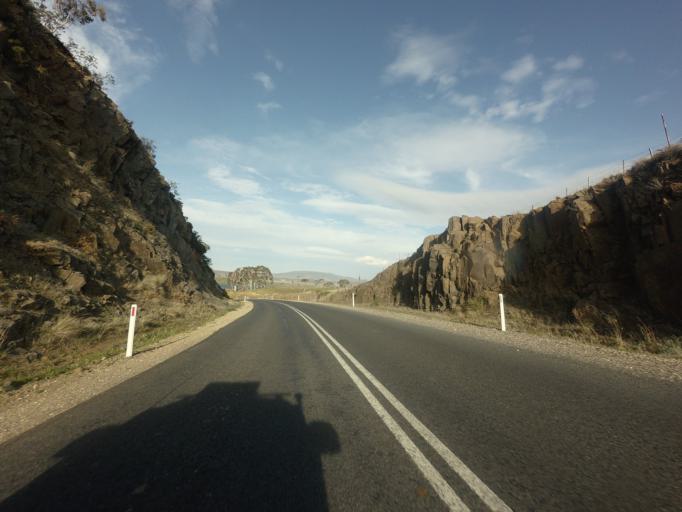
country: AU
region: Tasmania
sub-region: Derwent Valley
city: New Norfolk
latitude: -42.3463
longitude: 146.9825
